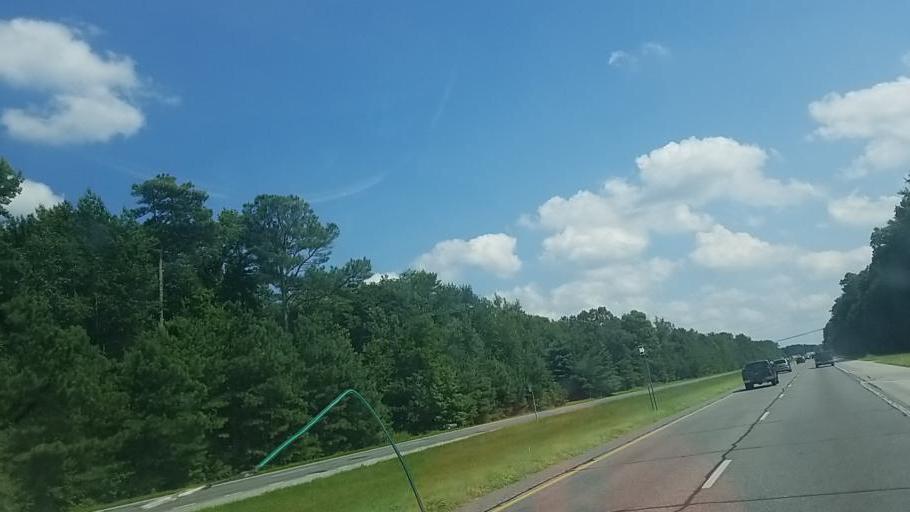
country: US
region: Delaware
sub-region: Sussex County
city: Georgetown
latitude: 38.7340
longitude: -75.4200
